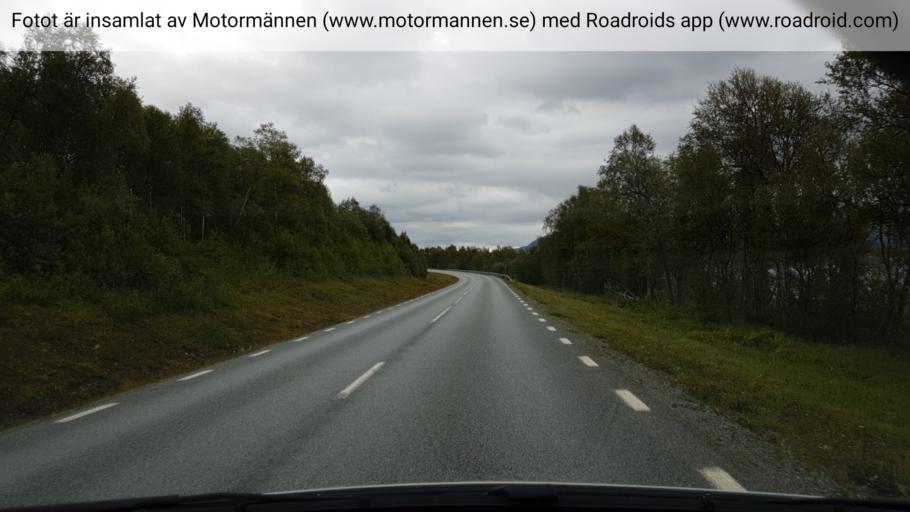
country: NO
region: Nordland
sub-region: Rana
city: Mo i Rana
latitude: 66.0452
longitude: 14.9755
